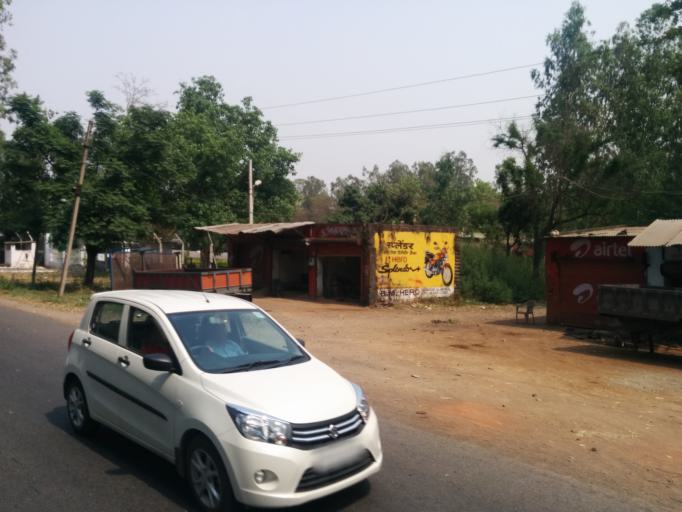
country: IN
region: Punjab
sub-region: Pathankot
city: Pathankot
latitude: 32.2722
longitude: 75.6039
